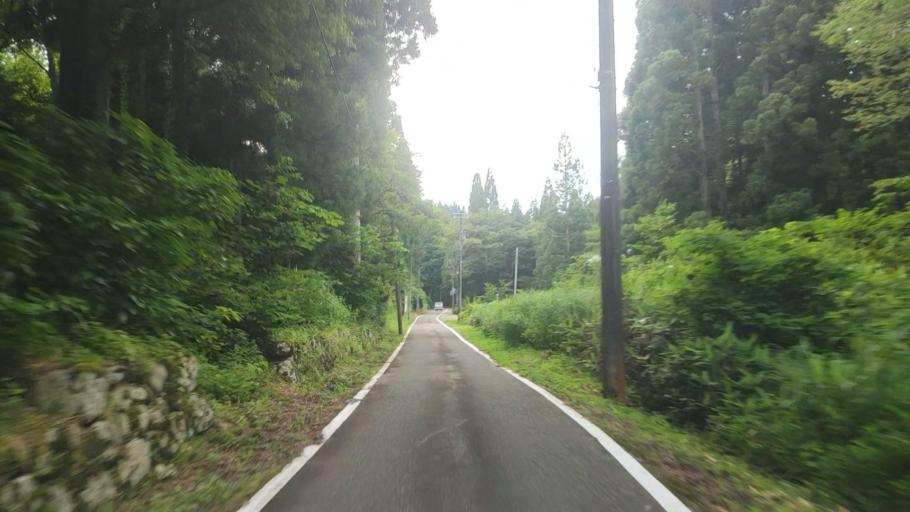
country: JP
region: Fukui
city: Katsuyama
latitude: 36.2020
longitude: 136.5251
